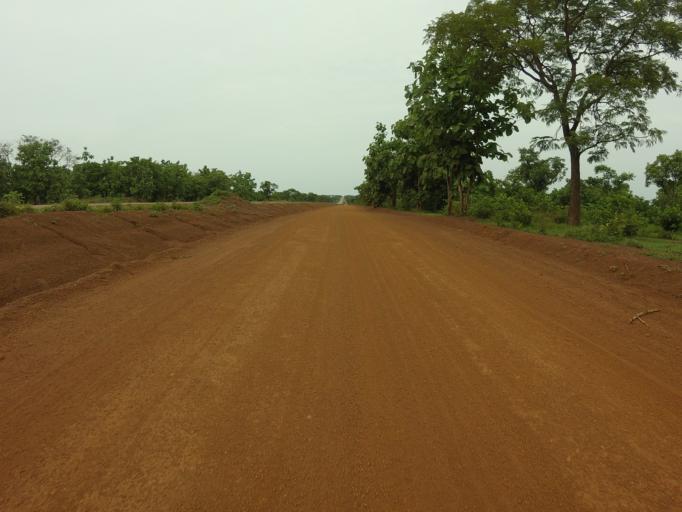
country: GH
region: Northern
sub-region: Yendi
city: Yendi
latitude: 9.0323
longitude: -0.0134
